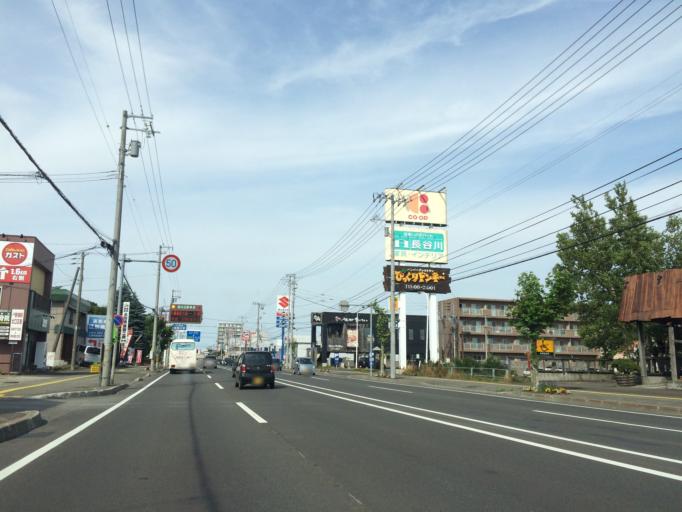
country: JP
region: Hokkaido
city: Ebetsu
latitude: 43.0901
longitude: 141.5194
